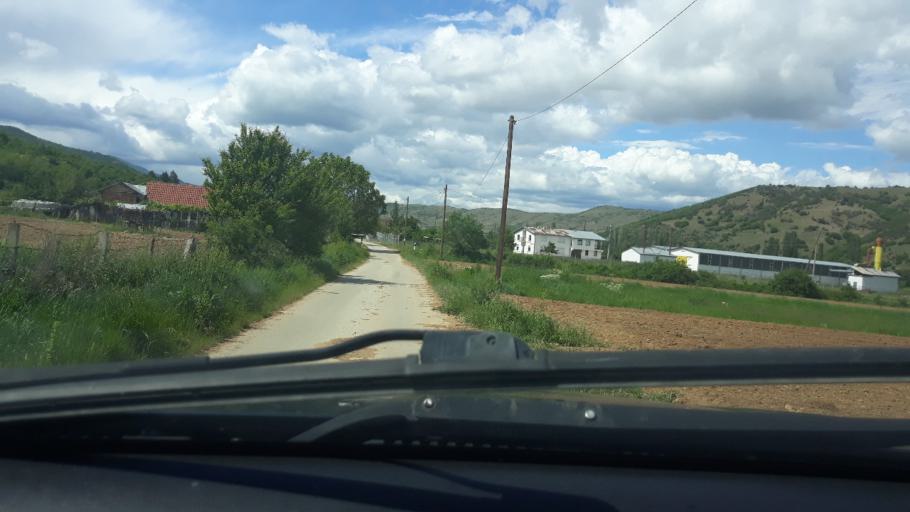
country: MK
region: Krivogastani
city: Krivogashtani
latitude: 41.3473
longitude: 21.2990
